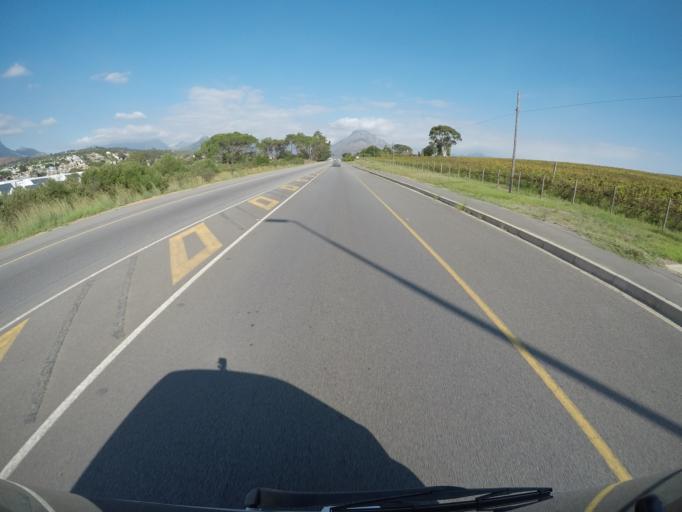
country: ZA
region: Western Cape
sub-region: Cape Winelands District Municipality
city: Stellenbosch
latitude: -33.9031
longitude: 18.8409
